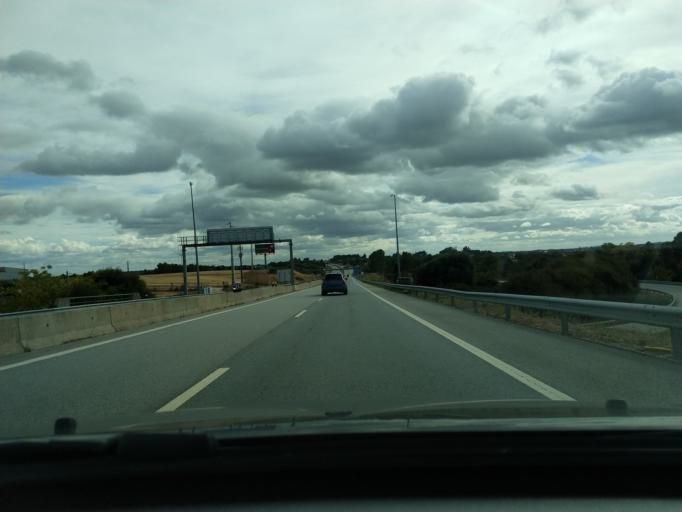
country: PT
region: Castelo Branco
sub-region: Concelho do Fundao
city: Fundao
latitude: 40.0376
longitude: -7.4693
